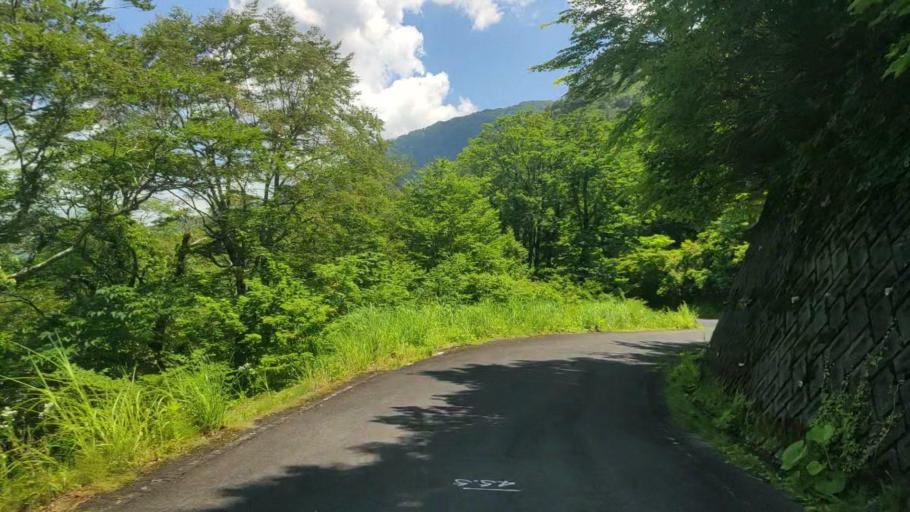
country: JP
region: Fukui
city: Ono
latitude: 35.7763
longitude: 136.5236
